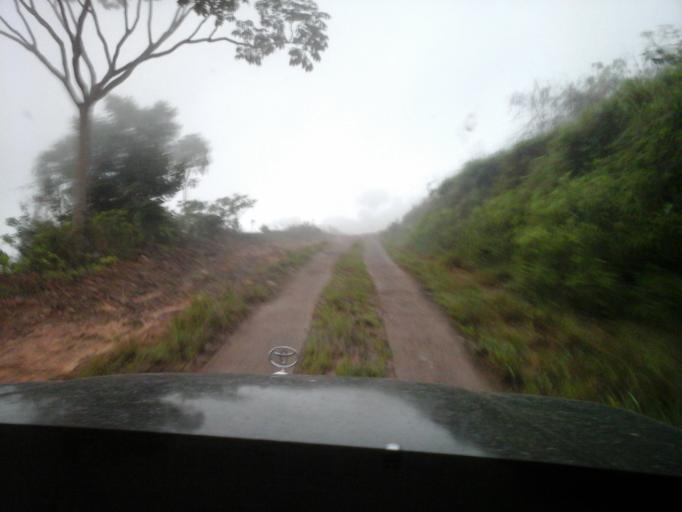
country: CO
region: Cesar
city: Agustin Codazzi
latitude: 9.9396
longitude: -73.1478
